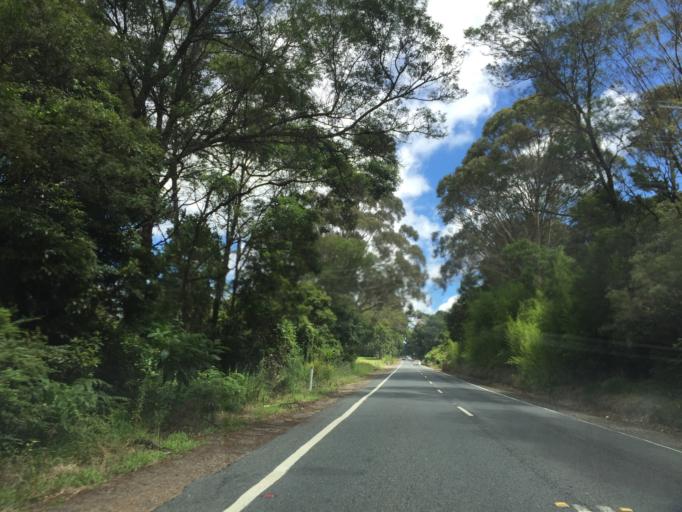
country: AU
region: New South Wales
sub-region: Blue Mountains Municipality
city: Hazelbrook
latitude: -33.5018
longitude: 150.5284
